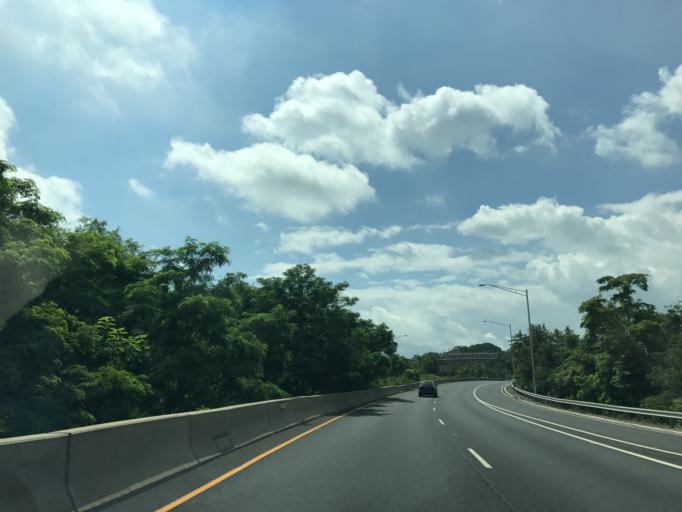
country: US
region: New Jersey
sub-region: Morris County
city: Morris Plains
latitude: 40.8088
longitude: -74.4465
